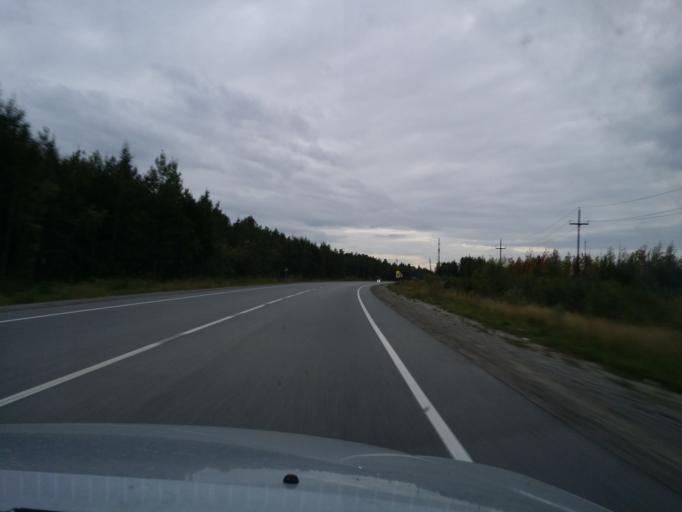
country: RU
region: Khanty-Mansiyskiy Avtonomnyy Okrug
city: Izluchinsk
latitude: 61.0140
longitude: 76.7968
